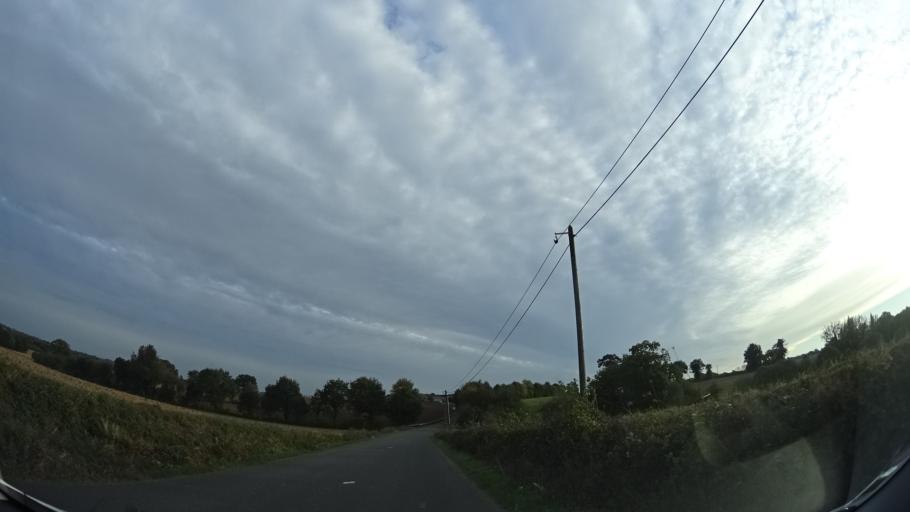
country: FR
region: Brittany
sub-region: Departement d'Ille-et-Vilaine
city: Geveze
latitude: 48.1948
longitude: -1.7937
